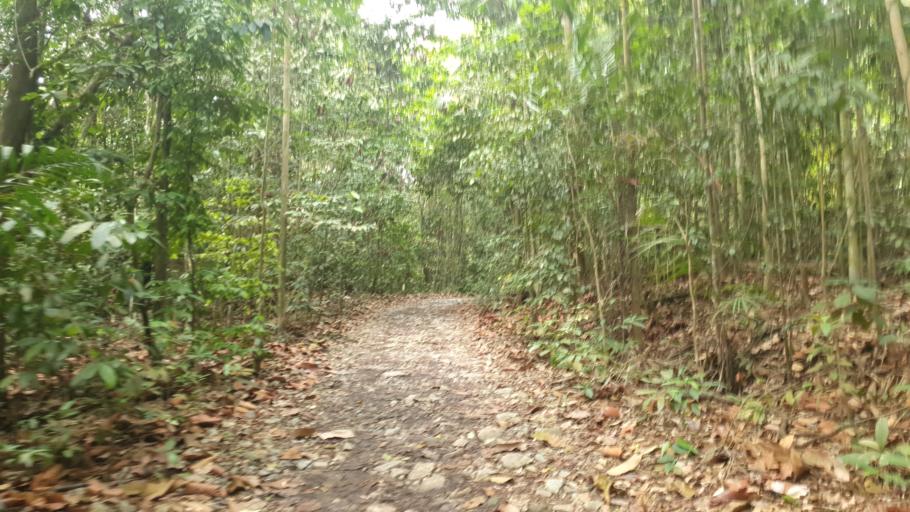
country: SG
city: Singapore
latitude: 1.3573
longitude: 103.8123
